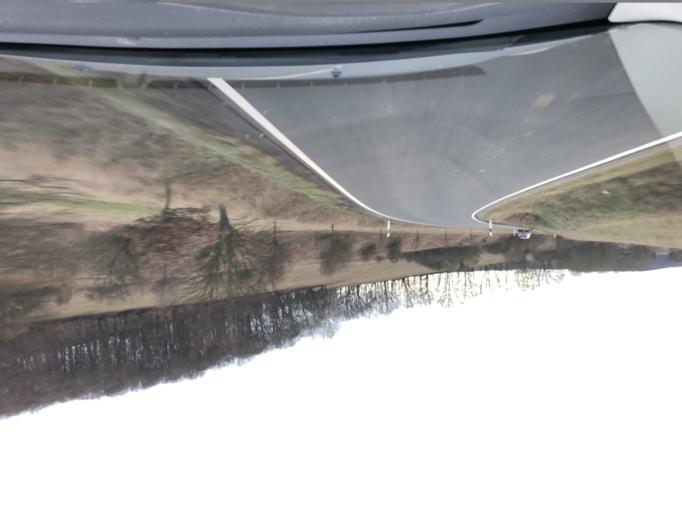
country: DE
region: Saxony-Anhalt
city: Balgstadt
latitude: 51.2052
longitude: 11.7156
